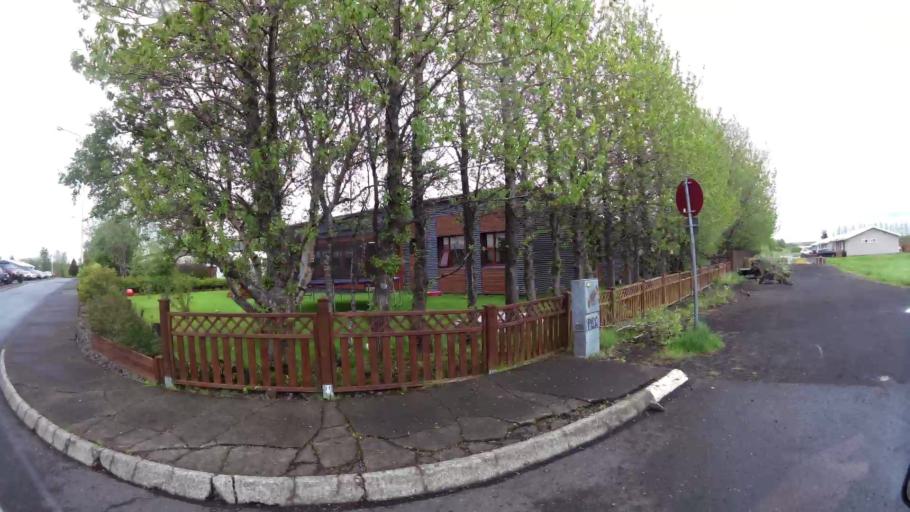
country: IS
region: South
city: Vestmannaeyjar
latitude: 63.8371
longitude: -20.3980
